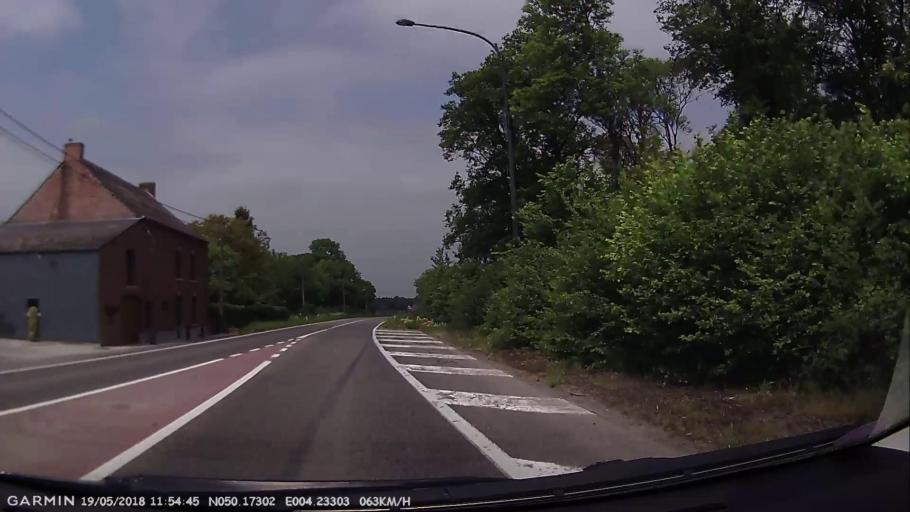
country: BE
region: Wallonia
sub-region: Province du Hainaut
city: Beaumont
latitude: 50.1731
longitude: 4.2329
